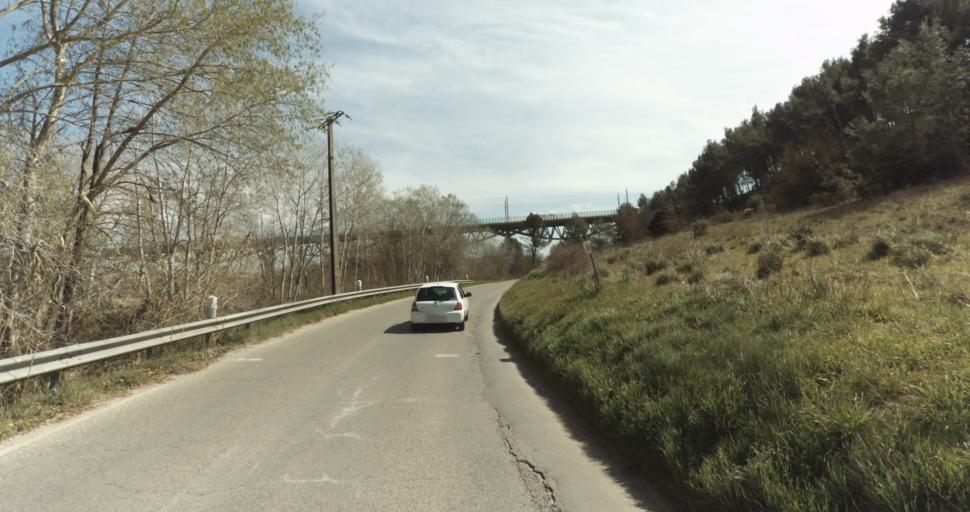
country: FR
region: Provence-Alpes-Cote d'Azur
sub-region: Departement des Bouches-du-Rhone
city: Ventabren
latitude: 43.5134
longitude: 5.3219
